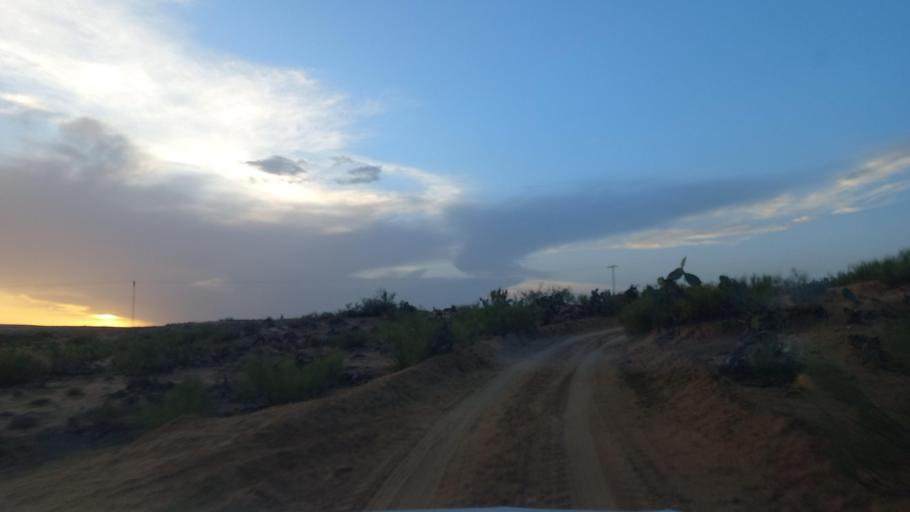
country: TN
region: Al Qasrayn
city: Kasserine
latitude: 35.2066
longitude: 9.0535
